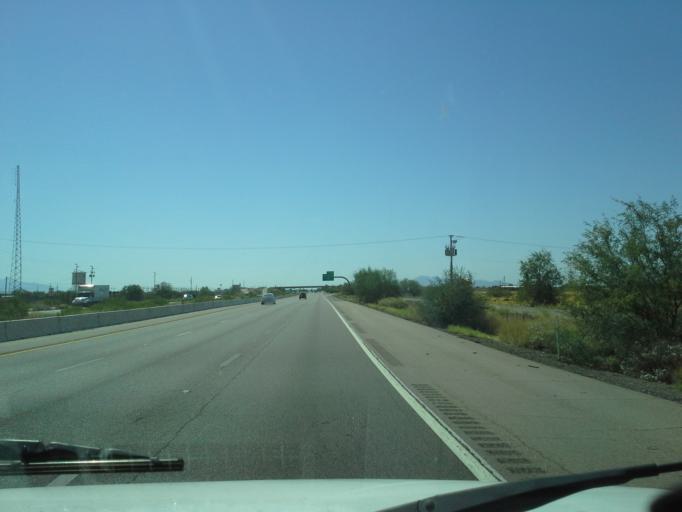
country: US
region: Arizona
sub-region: Pima County
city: Avra Valley
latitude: 32.5793
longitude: -111.3284
